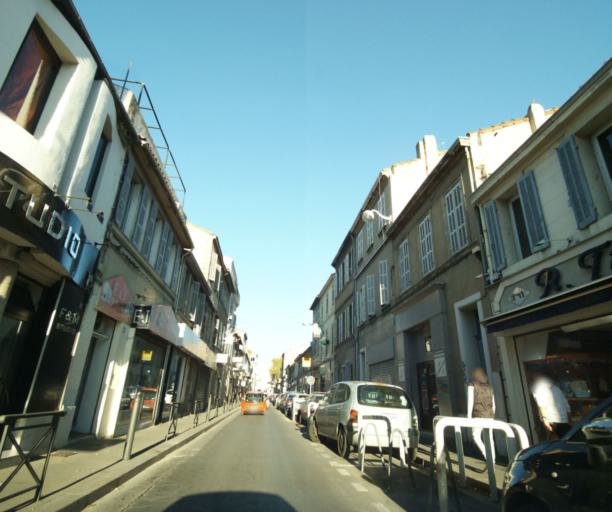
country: FR
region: Provence-Alpes-Cote d'Azur
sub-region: Departement des Bouches-du-Rhone
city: Marseille 13
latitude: 43.3182
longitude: 5.4068
